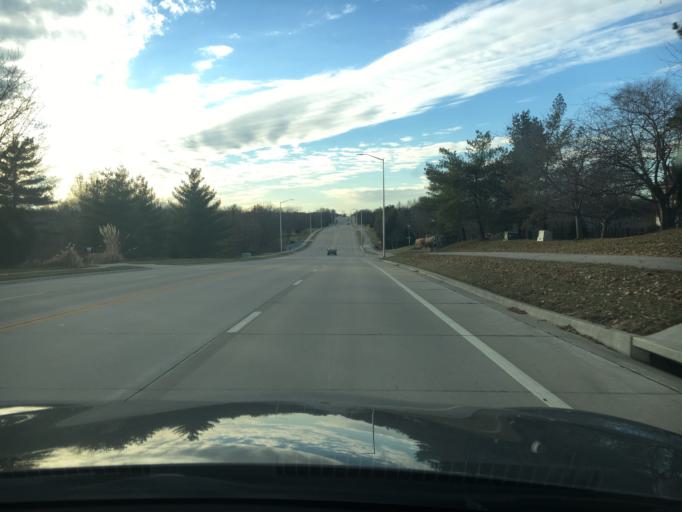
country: US
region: Kansas
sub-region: Johnson County
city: Leawood
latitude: 38.8693
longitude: -94.6358
